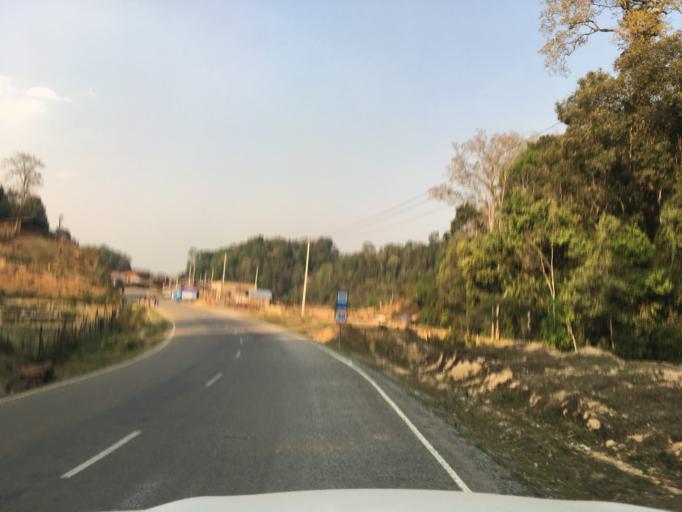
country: LA
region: Houaphan
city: Xam Nua
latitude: 20.5926
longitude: 104.0670
